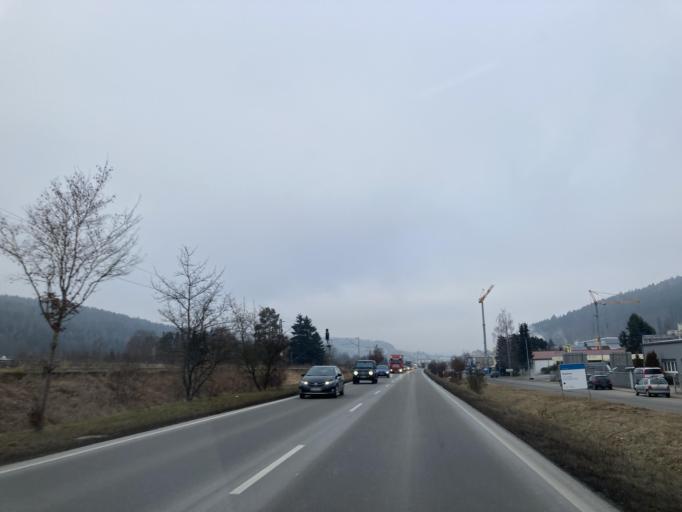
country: DE
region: Baden-Wuerttemberg
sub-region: Freiburg Region
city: Wurmlingen
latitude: 47.9693
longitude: 8.7871
